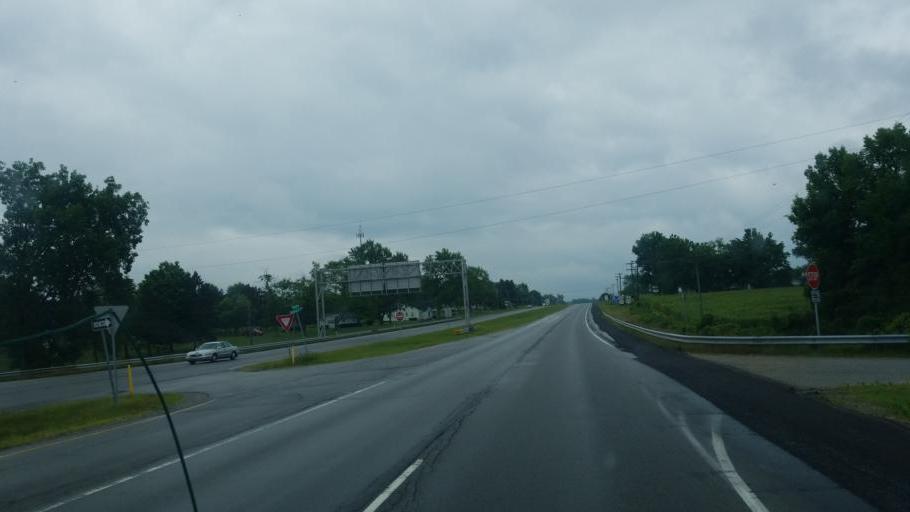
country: US
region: Indiana
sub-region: Allen County
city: New Haven
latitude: 40.9760
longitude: -85.0819
